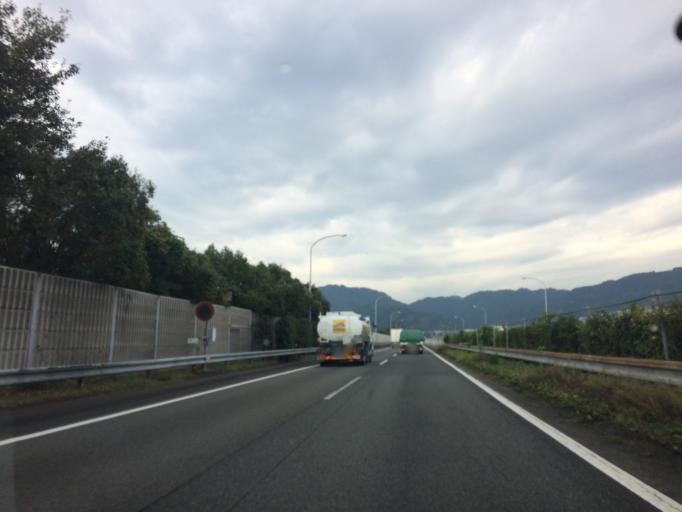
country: JP
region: Shizuoka
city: Shizuoka-shi
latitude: 34.9378
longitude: 138.3784
